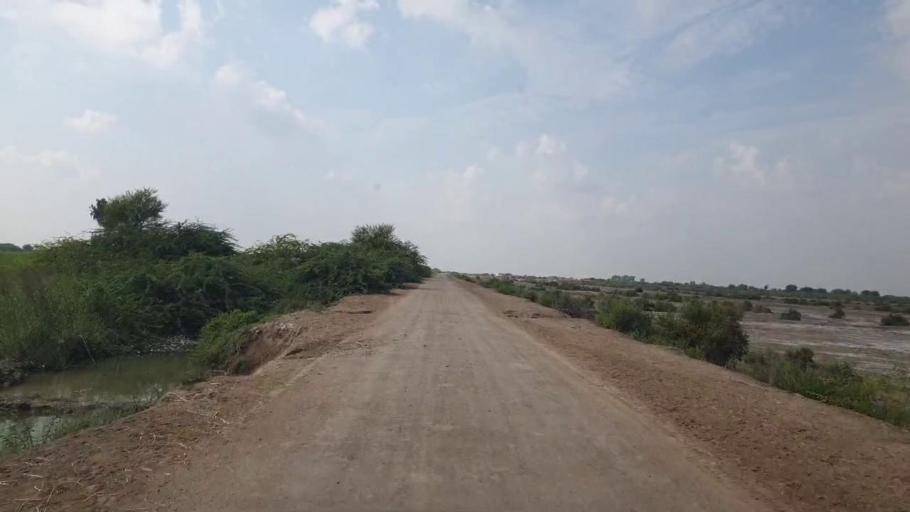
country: PK
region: Sindh
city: Badin
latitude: 24.5065
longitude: 68.6364
